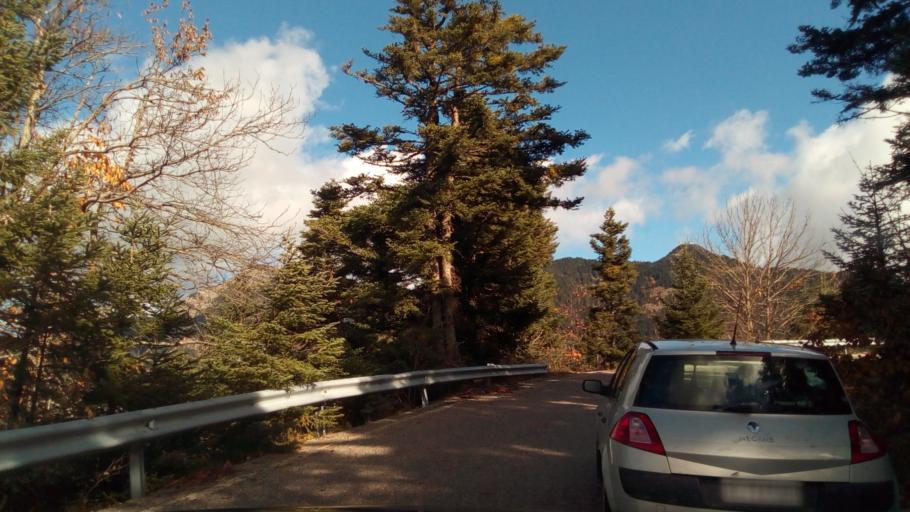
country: GR
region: West Greece
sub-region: Nomos Aitolias kai Akarnanias
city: Nafpaktos
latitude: 38.5881
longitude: 21.9367
